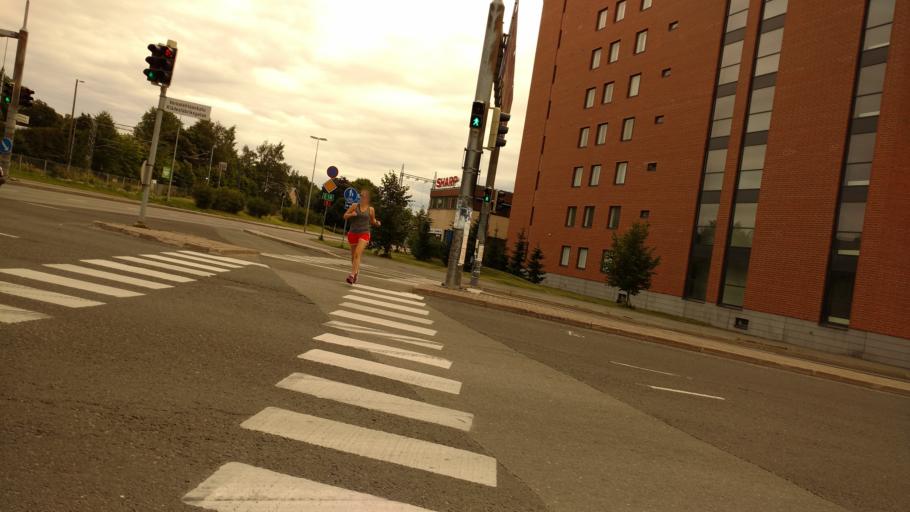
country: FI
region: Varsinais-Suomi
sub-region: Turku
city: Turku
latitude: 60.4589
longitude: 22.2692
